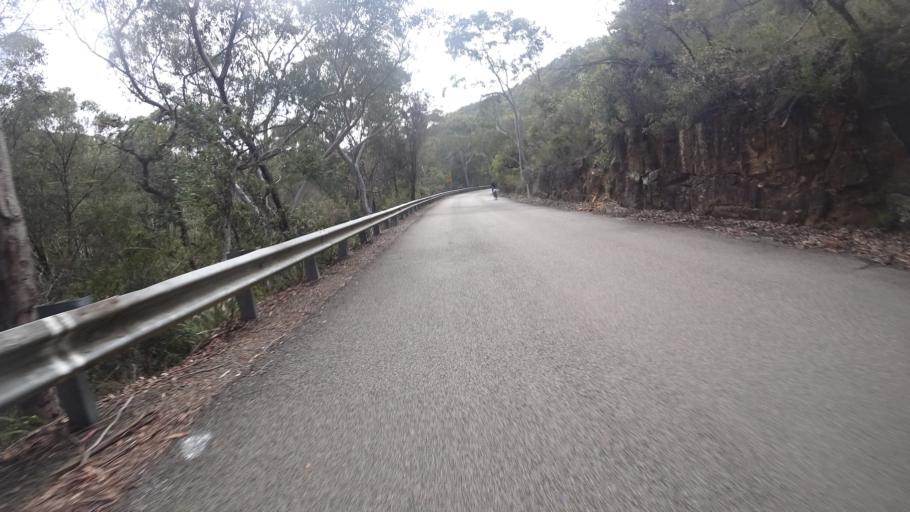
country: AU
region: New South Wales
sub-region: City of Sydney
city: North Turramurra
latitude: -33.6764
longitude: 151.1535
